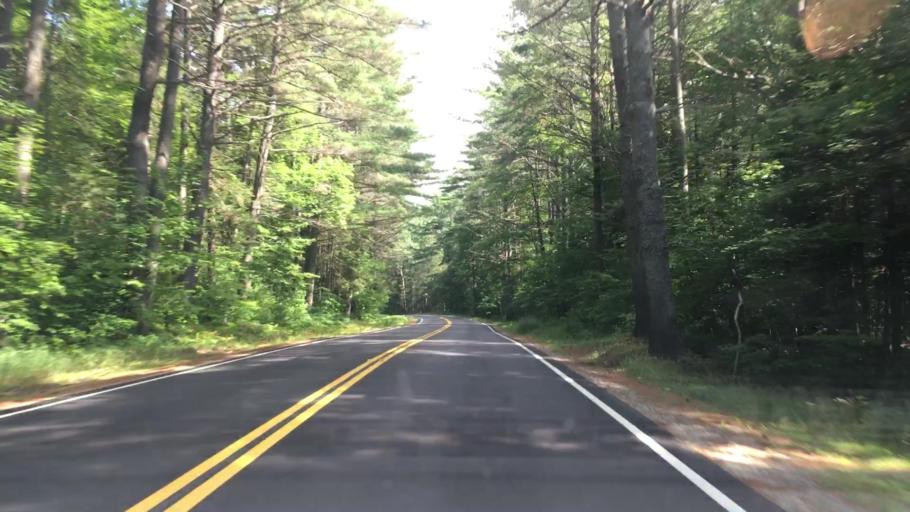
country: US
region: New Hampshire
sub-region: Grafton County
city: North Haverhill
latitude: 44.1032
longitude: -71.8654
